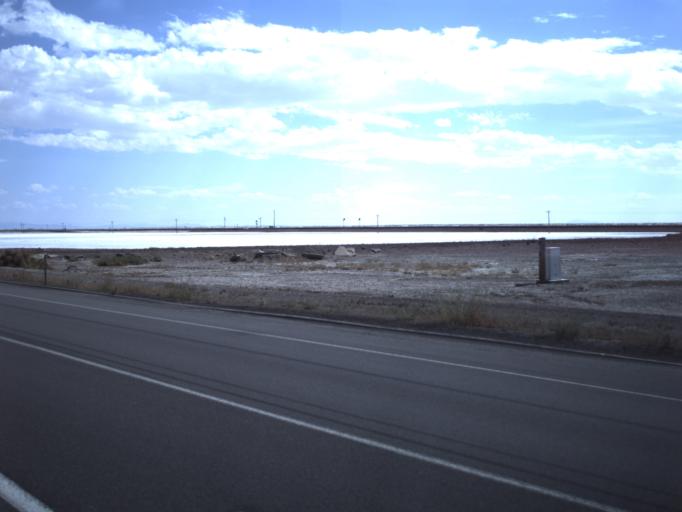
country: US
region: Utah
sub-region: Tooele County
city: Wendover
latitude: 40.7385
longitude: -113.8531
